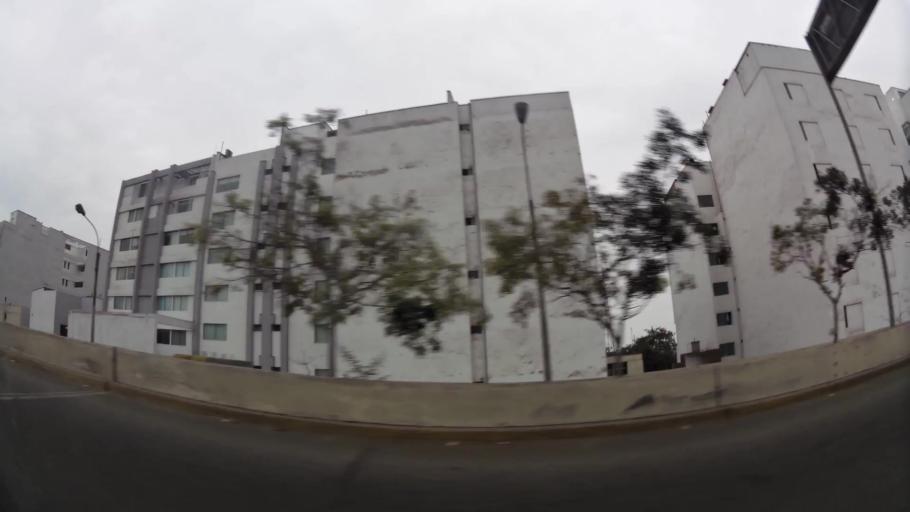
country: PE
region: Lima
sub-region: Lima
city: San Luis
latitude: -12.0984
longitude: -76.9803
